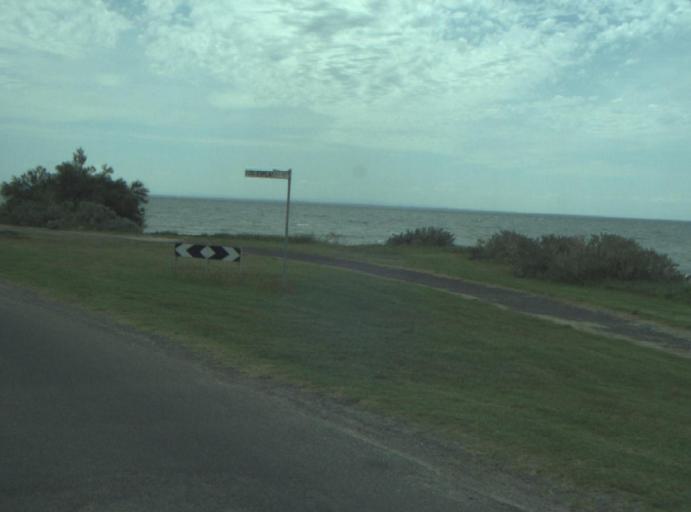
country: AU
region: Victoria
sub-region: Greater Geelong
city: Clifton Springs
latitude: -38.1210
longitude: 144.6927
